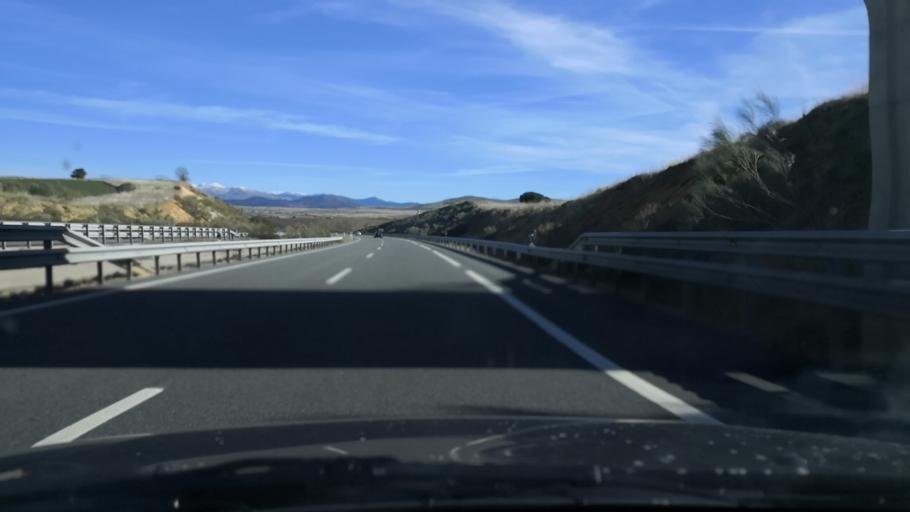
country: ES
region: Castille and Leon
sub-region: Provincia de Segovia
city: Villacastin
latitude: 40.7511
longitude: -4.4645
